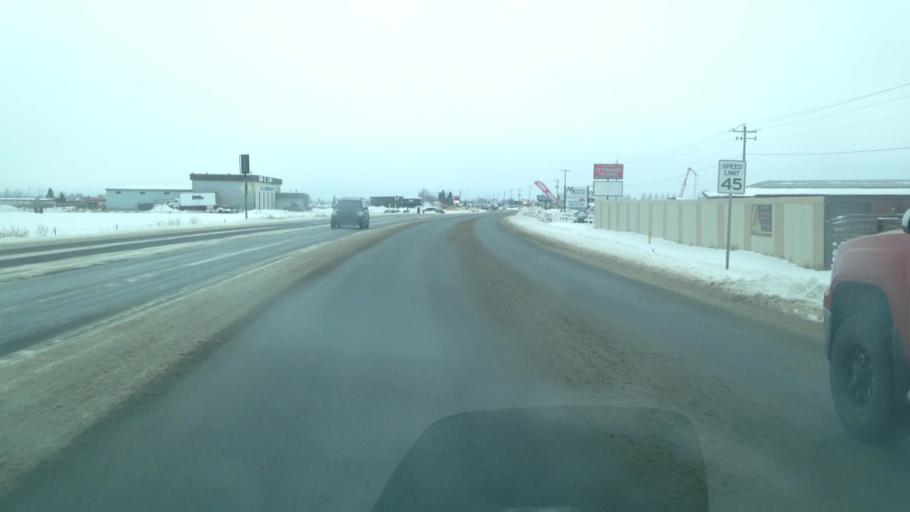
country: US
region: Idaho
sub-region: Madison County
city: Rexburg
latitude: 43.8426
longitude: -111.7783
